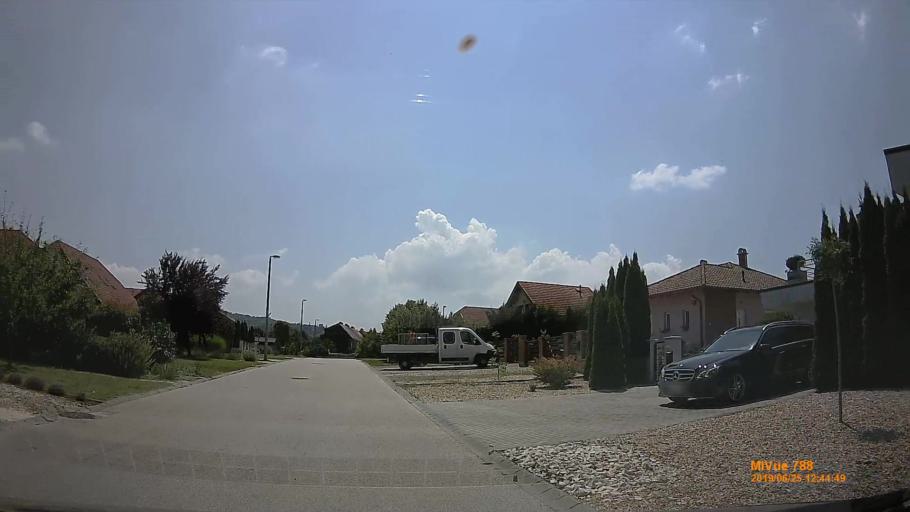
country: HU
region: Komarom-Esztergom
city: Esztergom
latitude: 47.8095
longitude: 18.7459
